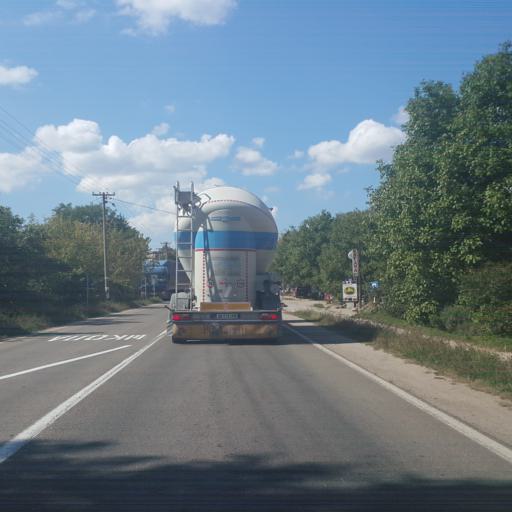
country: RS
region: Central Serbia
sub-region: Pirotski Okrug
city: Bela Palanka
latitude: 43.2716
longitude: 22.2366
